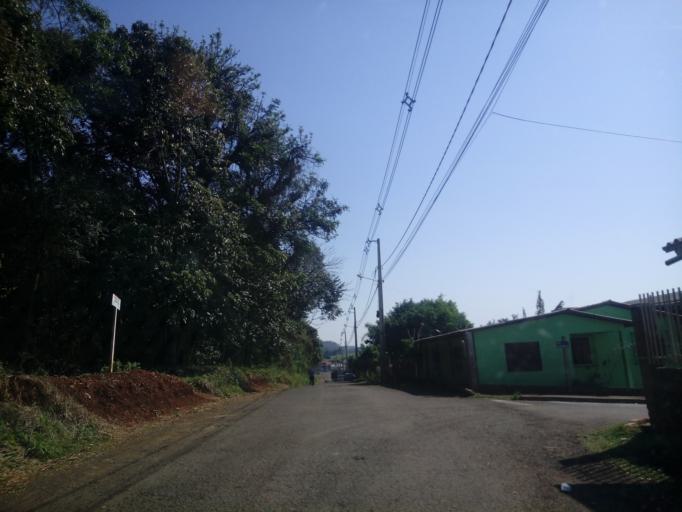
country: BR
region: Santa Catarina
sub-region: Chapeco
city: Chapeco
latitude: -27.0931
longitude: -52.6752
